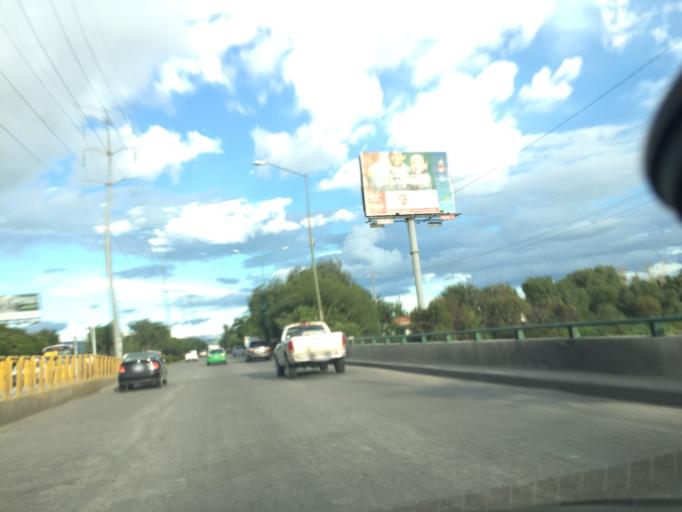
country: MX
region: Guanajuato
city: Leon
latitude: 21.1543
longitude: -101.6822
